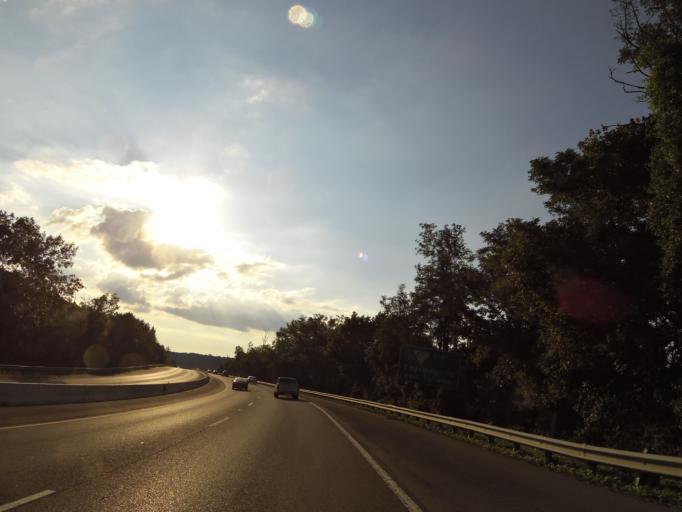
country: US
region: Tennessee
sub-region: Anderson County
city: Oak Ridge
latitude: 35.9905
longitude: -84.1906
